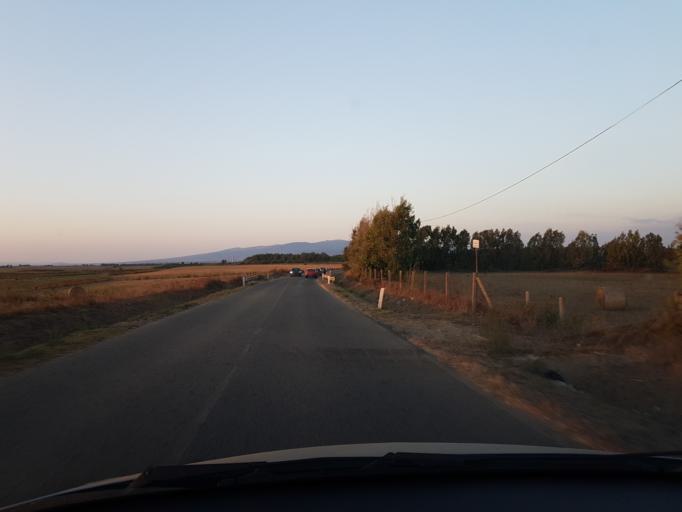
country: IT
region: Sardinia
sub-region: Provincia di Oristano
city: Nurachi
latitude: 39.9891
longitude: 8.4601
